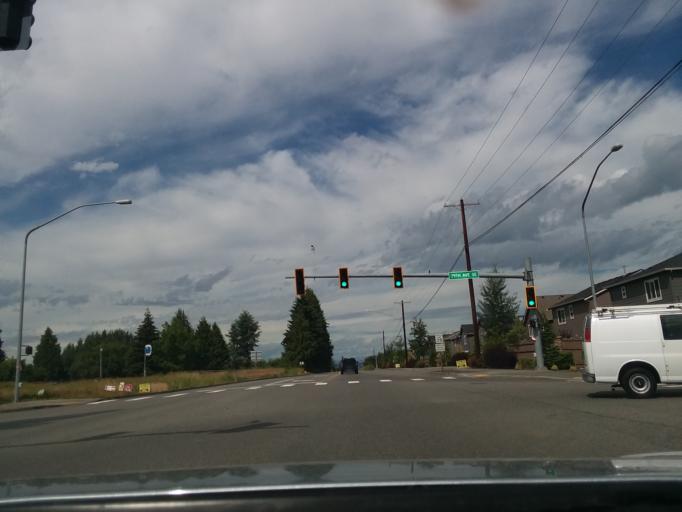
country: US
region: Washington
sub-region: Snohomish County
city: West Lake Stevens
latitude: 47.9781
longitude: -122.1247
